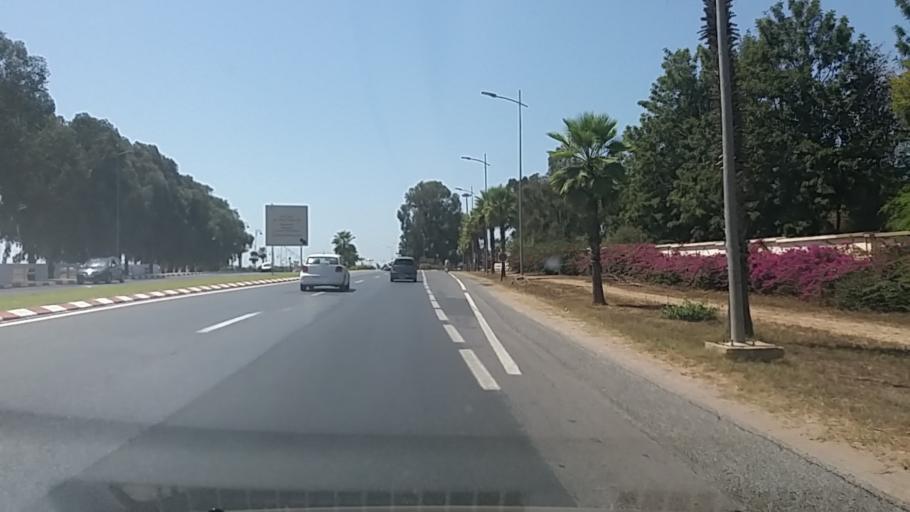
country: MA
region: Rabat-Sale-Zemmour-Zaer
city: Sale
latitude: 34.0308
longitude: -6.7519
